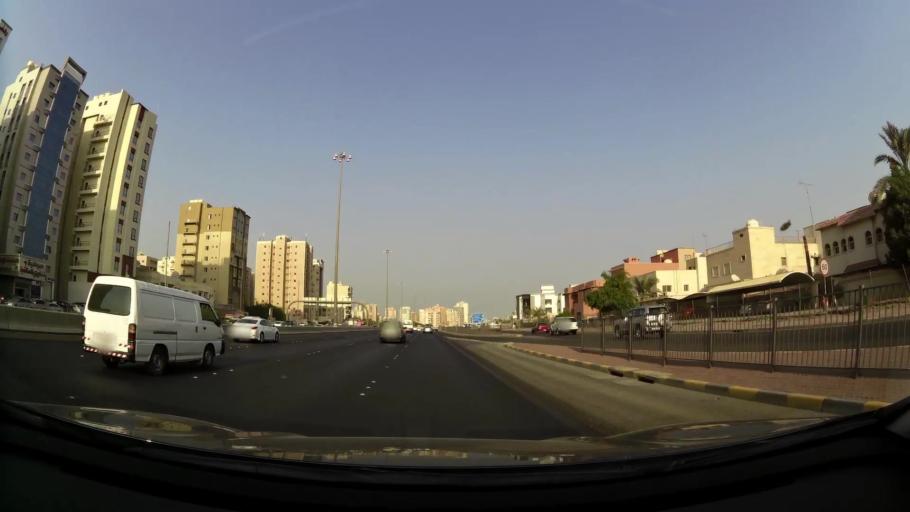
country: KW
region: Muhafazat Hawalli
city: Ar Rumaythiyah
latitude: 29.3211
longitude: 48.0625
